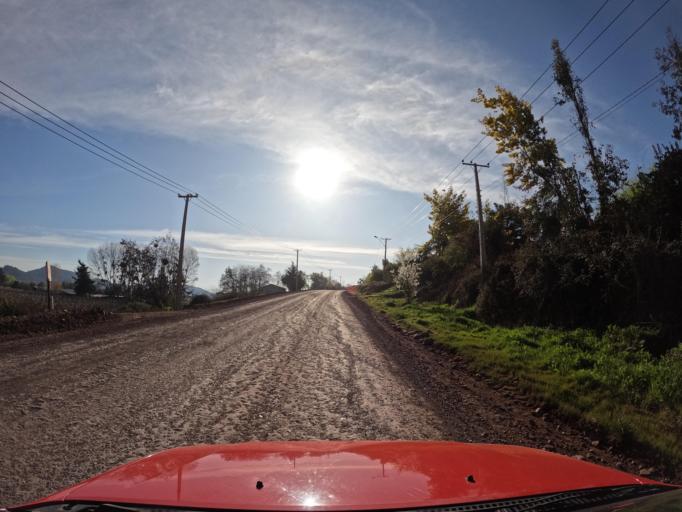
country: CL
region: Maule
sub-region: Provincia de Curico
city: Teno
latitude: -34.9660
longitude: -70.9503
